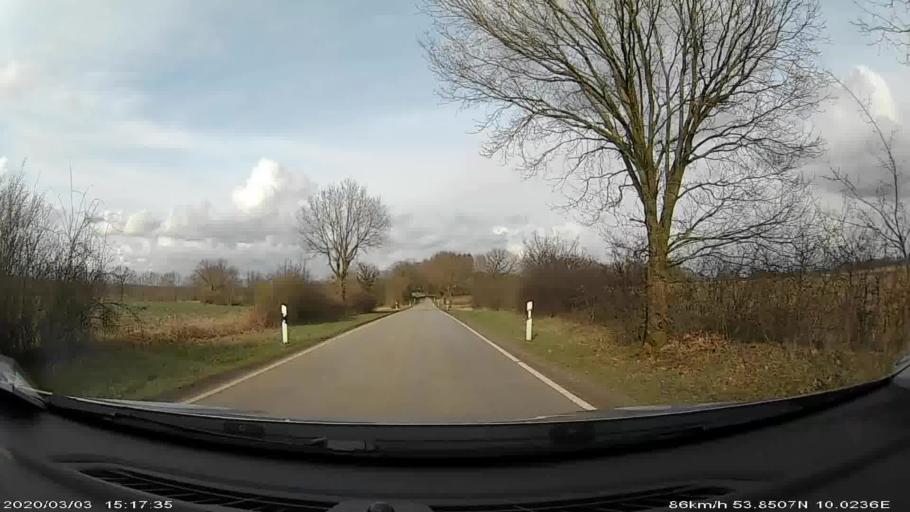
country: DE
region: Schleswig-Holstein
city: Kattendorf
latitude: 53.8502
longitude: 10.0235
